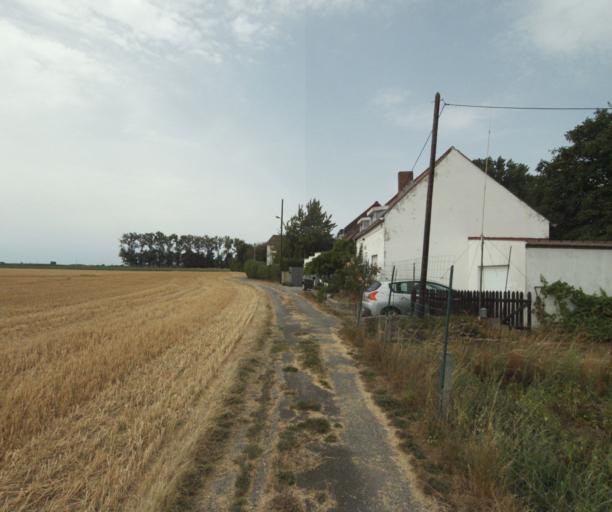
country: BE
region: Wallonia
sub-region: Province du Hainaut
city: Estaimpuis
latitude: 50.6979
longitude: 3.2551
